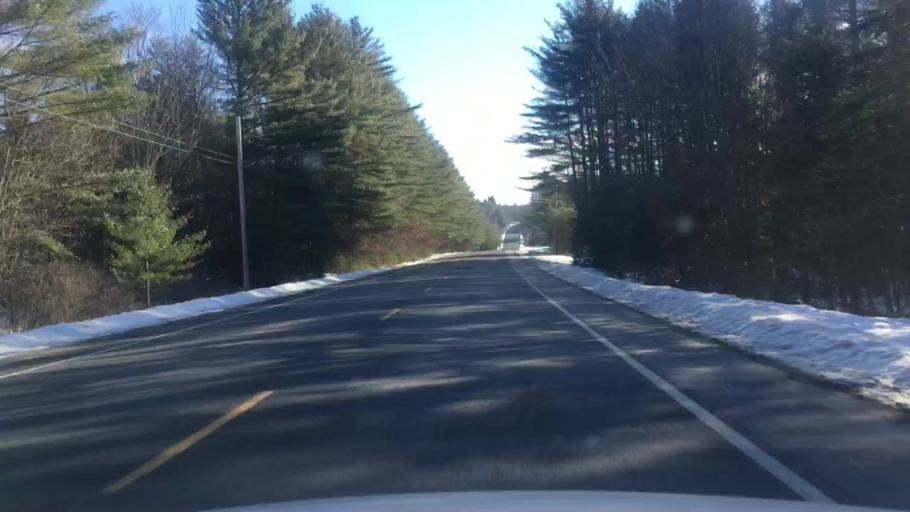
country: US
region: Maine
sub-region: Somerset County
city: Madison
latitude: 44.9070
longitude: -69.8165
